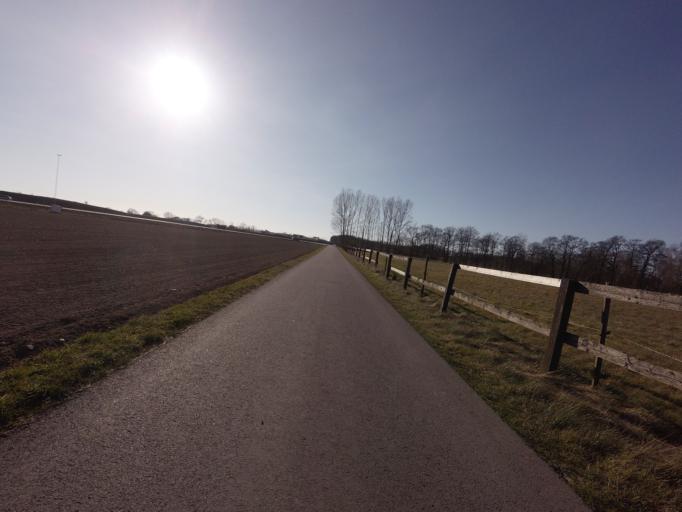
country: SE
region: Skane
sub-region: Helsingborg
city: Helsingborg
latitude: 56.0997
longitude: 12.6699
